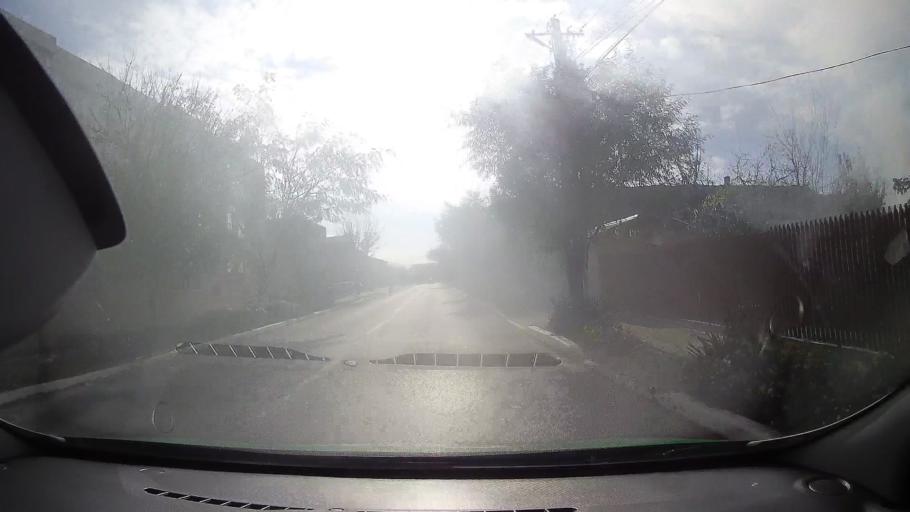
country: RO
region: Tulcea
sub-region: Comuna Sarichioi
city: Sarichioi
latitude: 44.9457
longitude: 28.8531
